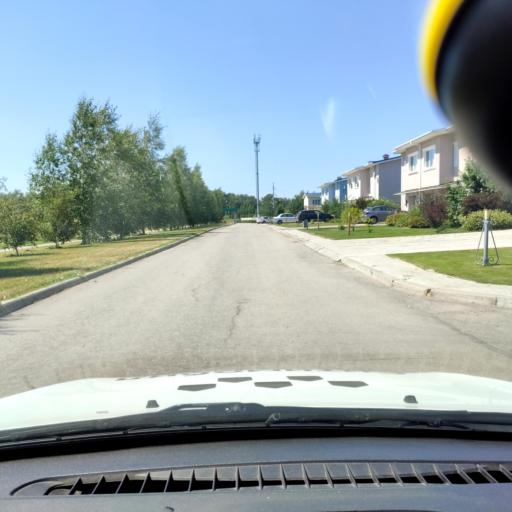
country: RU
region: Samara
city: Tol'yatti
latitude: 53.6186
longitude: 49.3166
